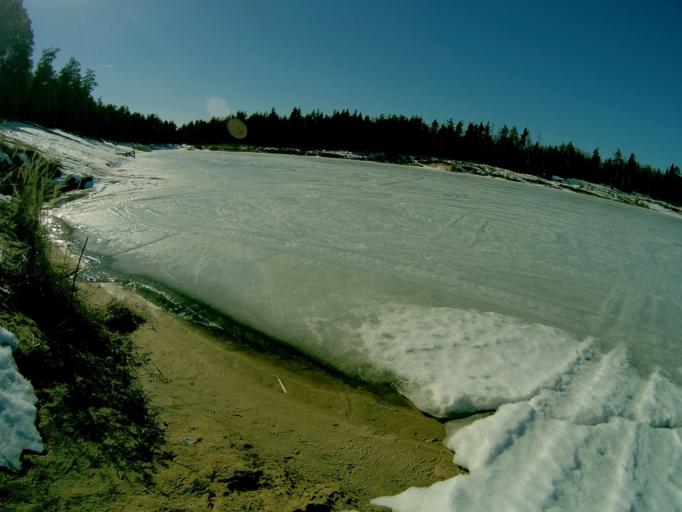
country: RU
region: Vladimir
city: Golovino
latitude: 56.0336
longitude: 40.4120
